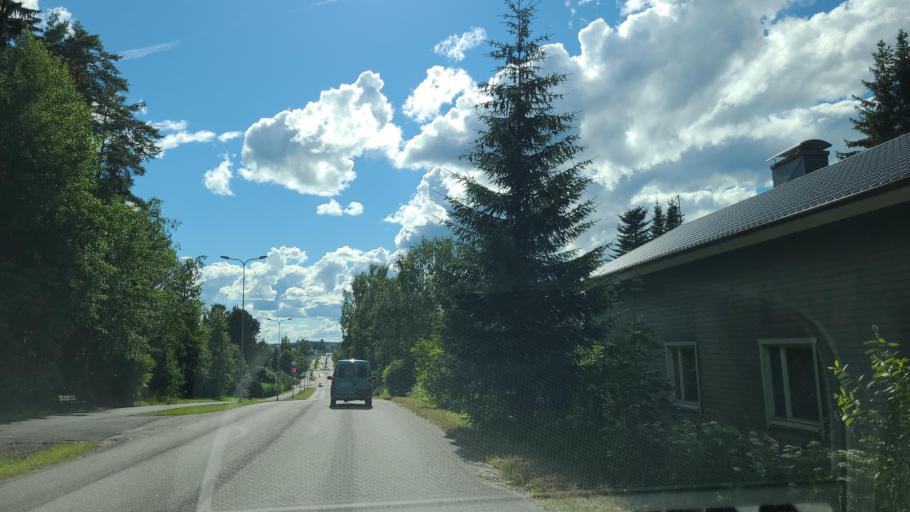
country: FI
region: Central Finland
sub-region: Jaemsae
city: Jaemsae
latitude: 61.8680
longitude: 25.2073
